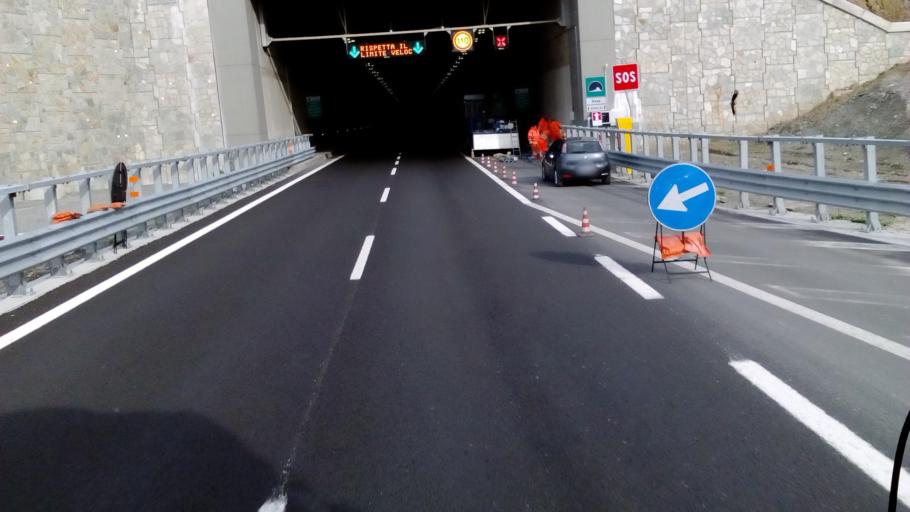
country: IT
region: Tuscany
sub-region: Province of Florence
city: Barberino di Mugello
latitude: 44.0732
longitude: 11.2388
